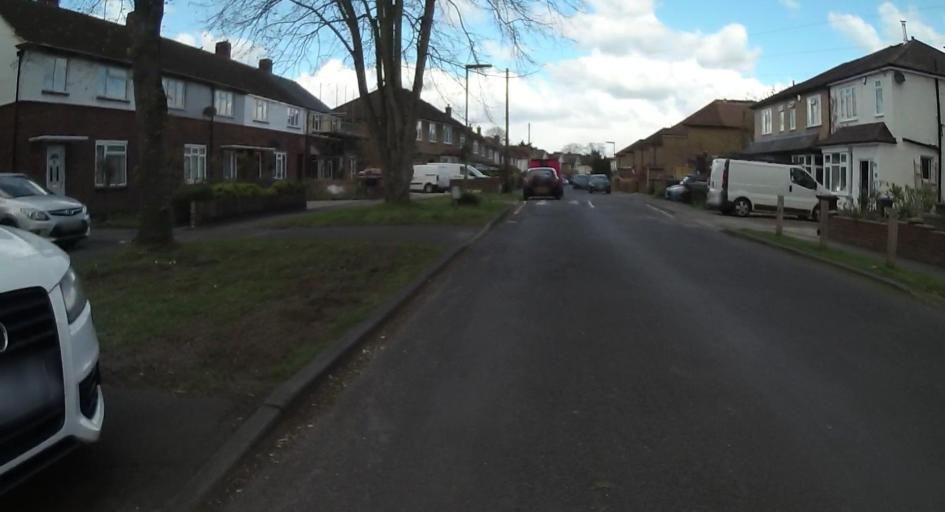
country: GB
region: England
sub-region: Surrey
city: Addlestone
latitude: 51.3701
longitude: -0.5007
